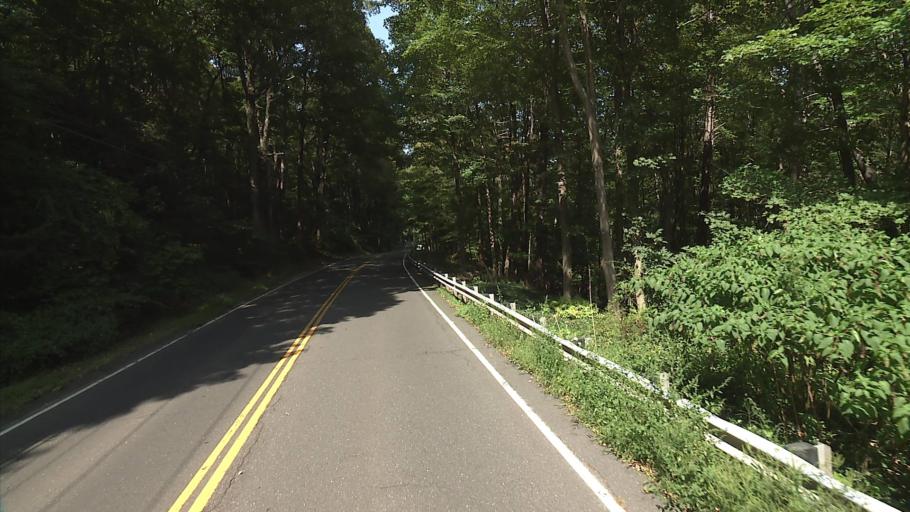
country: US
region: Connecticut
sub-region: Fairfield County
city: Georgetown
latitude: 41.2573
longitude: -73.3246
